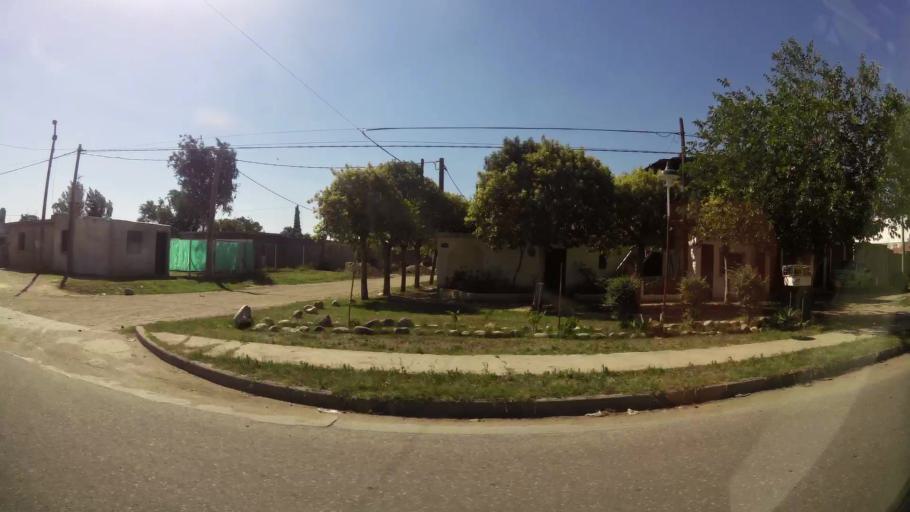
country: AR
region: Cordoba
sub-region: Departamento de Capital
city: Cordoba
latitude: -31.4166
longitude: -64.1453
